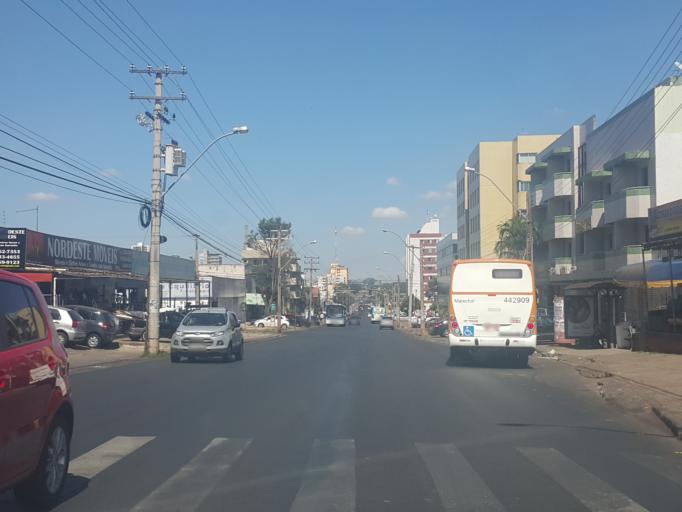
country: BR
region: Federal District
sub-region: Brasilia
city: Brasilia
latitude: -15.8259
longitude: -48.0633
